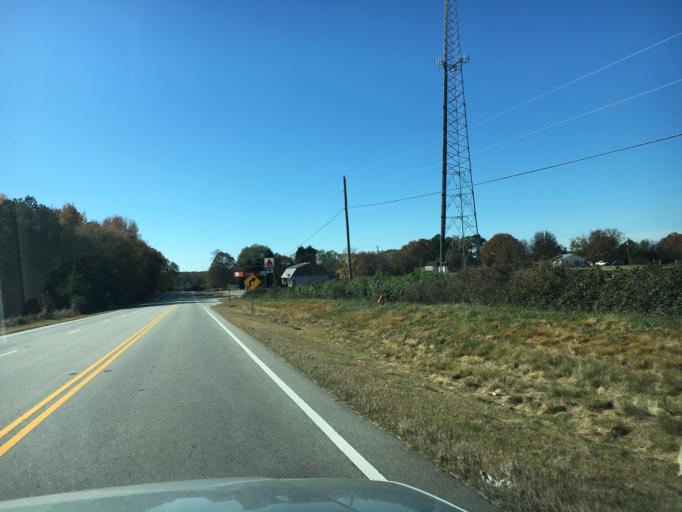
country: US
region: Georgia
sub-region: Hart County
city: Royston
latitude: 34.2889
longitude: -83.0520
